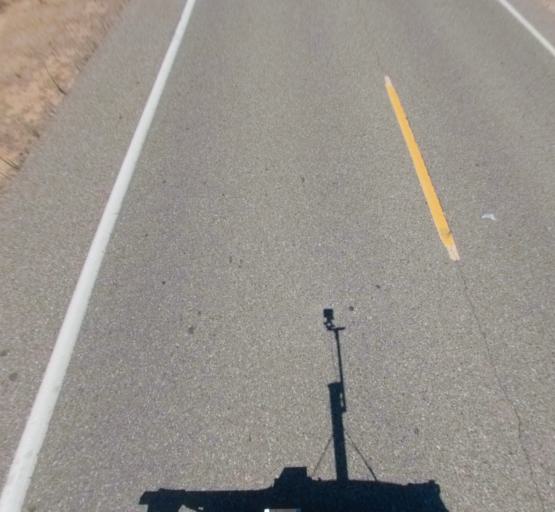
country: US
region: California
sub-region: Madera County
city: Fairmead
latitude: 37.0982
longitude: -120.1637
